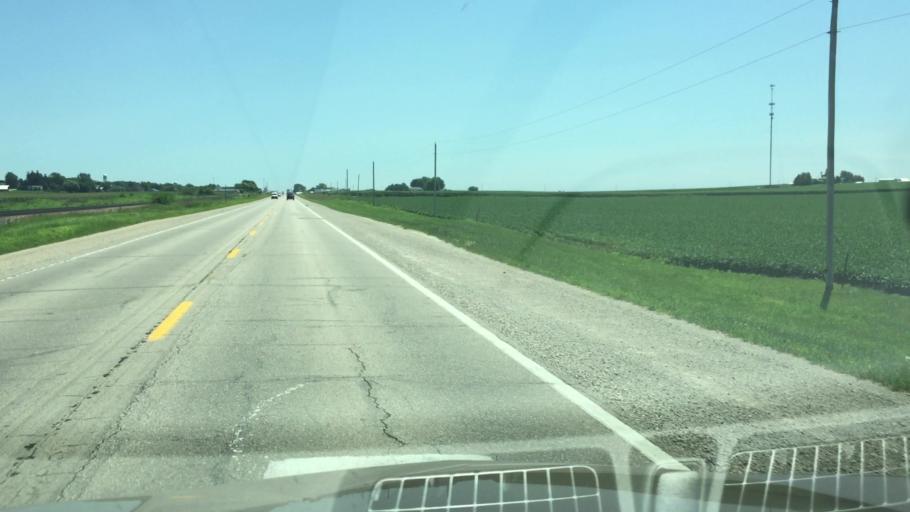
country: US
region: Iowa
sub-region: Cedar County
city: Mechanicsville
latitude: 41.9080
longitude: -91.2775
